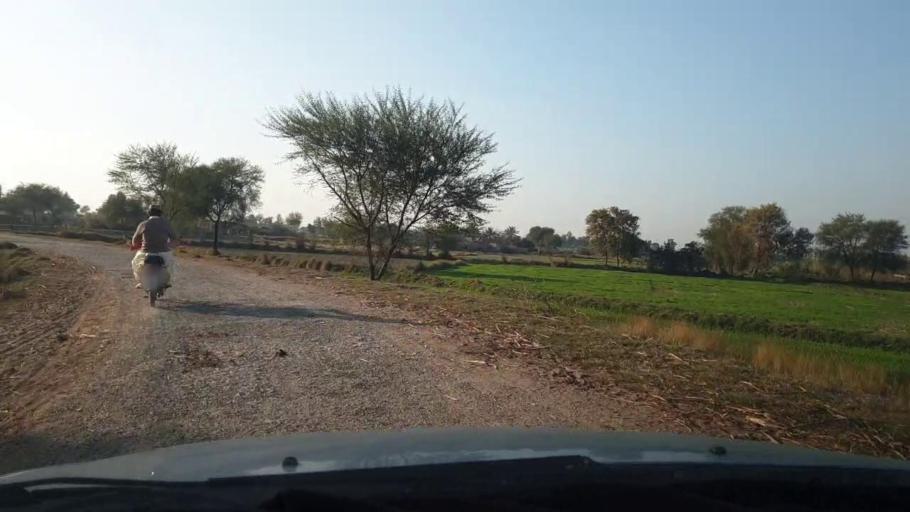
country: PK
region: Sindh
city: Mirpur Mathelo
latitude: 28.0018
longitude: 69.5144
